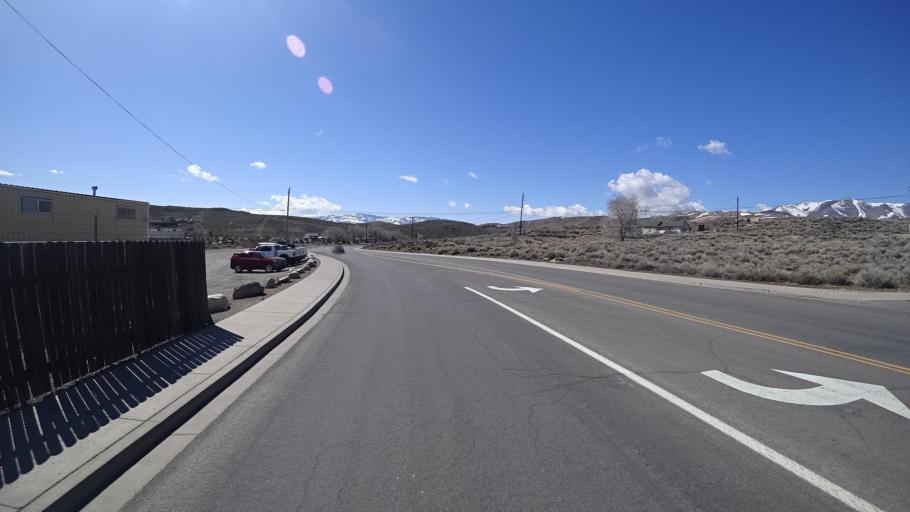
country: US
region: Nevada
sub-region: Washoe County
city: Golden Valley
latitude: 39.5847
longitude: -119.8263
